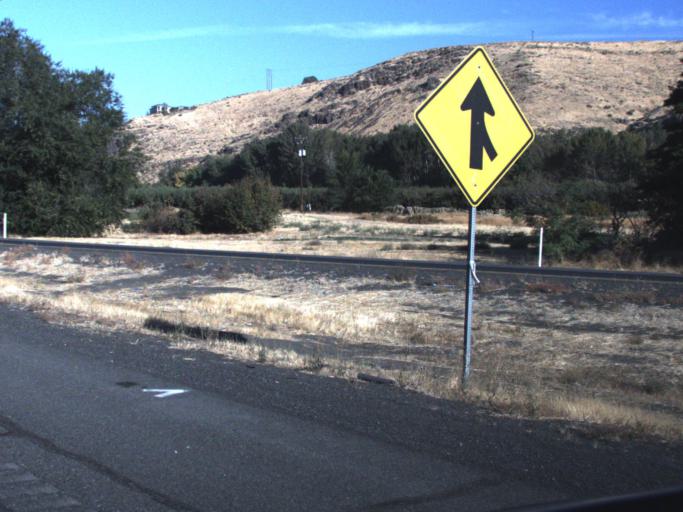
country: US
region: Washington
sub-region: Yakima County
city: West Valley
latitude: 46.6236
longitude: -120.5691
